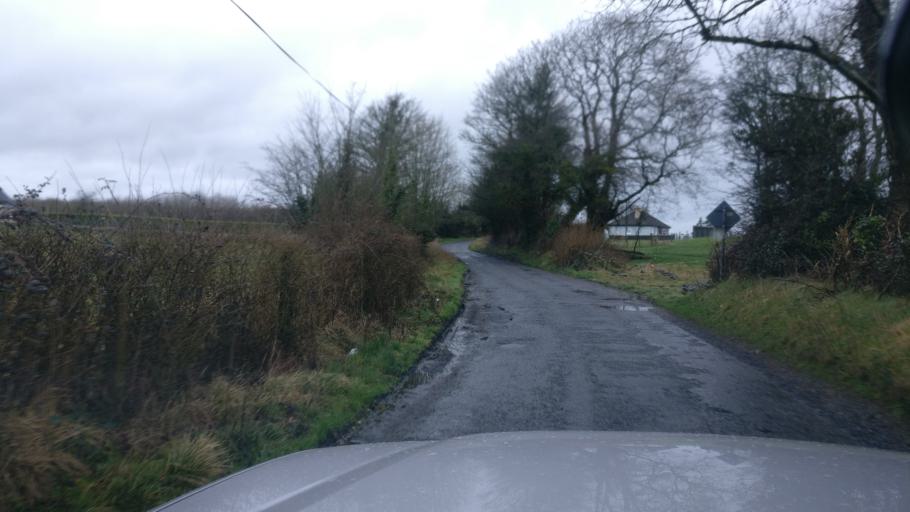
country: IE
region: Connaught
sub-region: County Galway
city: Ballinasloe
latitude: 53.2537
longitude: -8.3540
